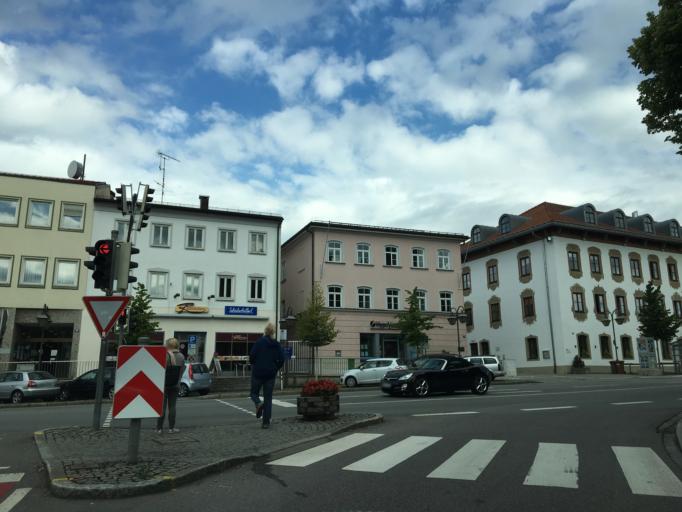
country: DE
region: Bavaria
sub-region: Upper Bavaria
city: Holzkirchen
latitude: 47.8767
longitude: 11.7014
